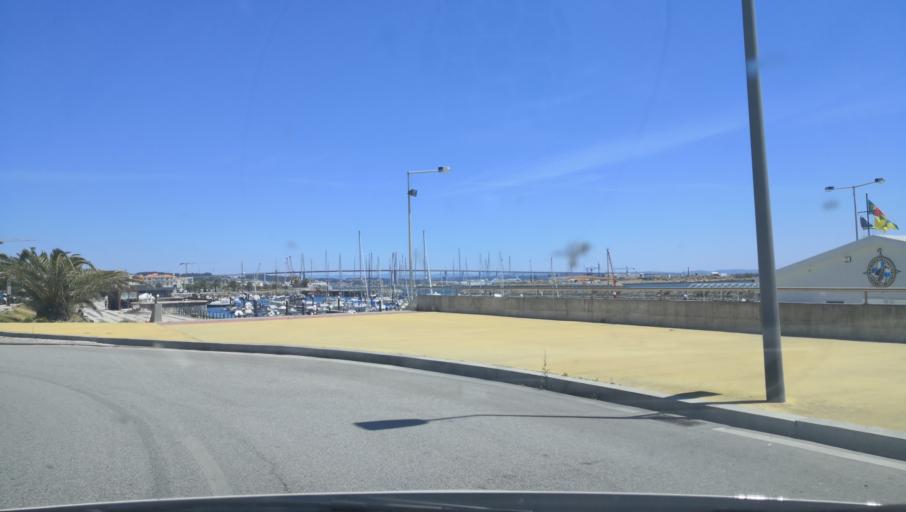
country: PT
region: Coimbra
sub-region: Figueira da Foz
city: Figueira da Foz
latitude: 40.1478
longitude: -8.8633
